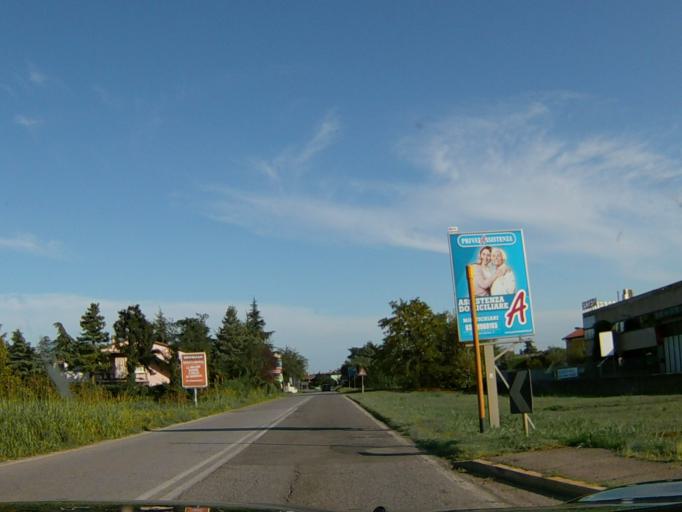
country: IT
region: Lombardy
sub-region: Provincia di Brescia
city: Molinetto
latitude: 45.4885
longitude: 10.3675
